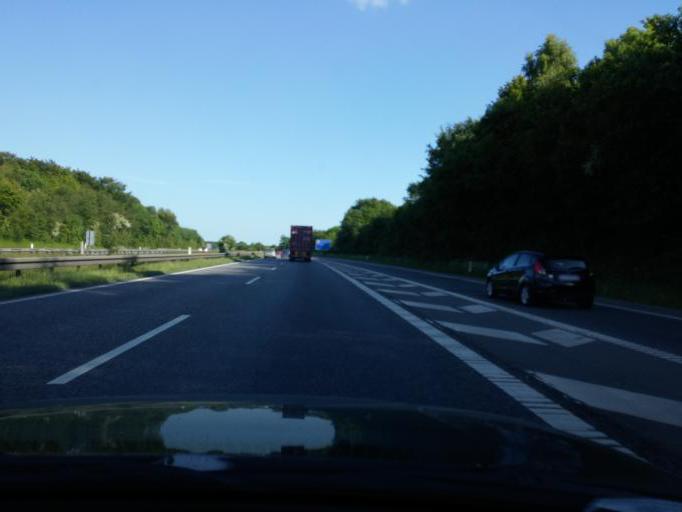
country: DK
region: South Denmark
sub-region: Kolding Kommune
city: Kolding
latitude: 55.4738
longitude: 9.4267
